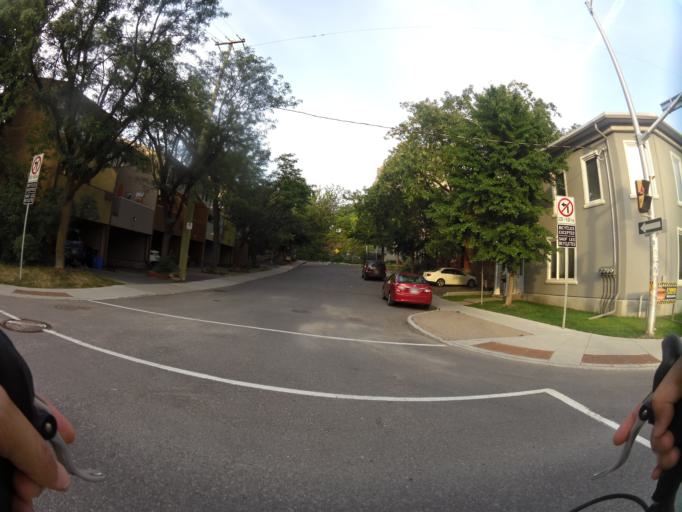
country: CA
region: Ontario
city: Ottawa
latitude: 45.4114
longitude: -75.7117
